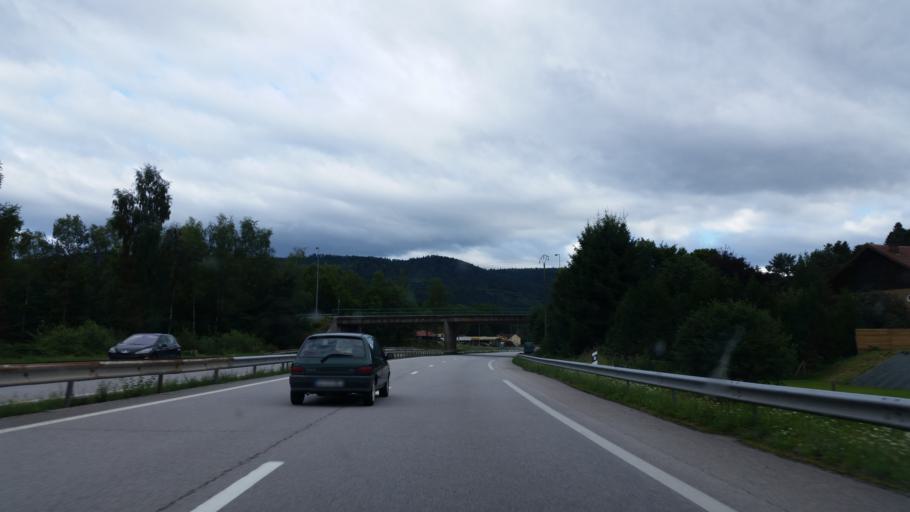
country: FR
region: Lorraine
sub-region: Departement des Vosges
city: Saint-Nabord
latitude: 48.0709
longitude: 6.5959
